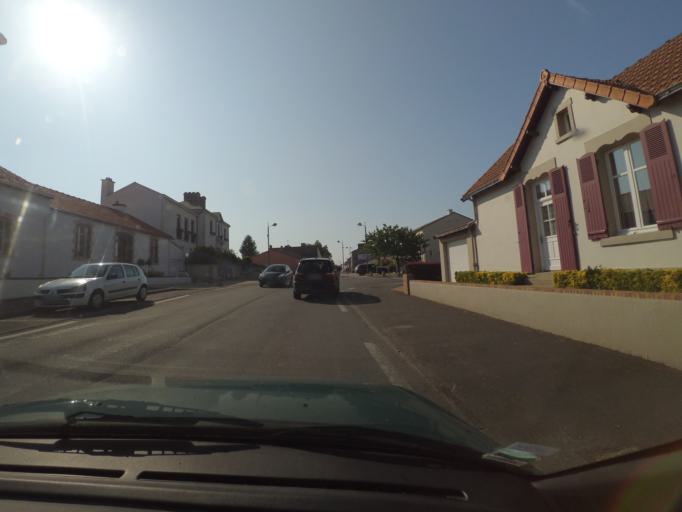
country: FR
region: Pays de la Loire
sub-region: Departement de la Loire-Atlantique
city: Le Pallet
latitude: 47.1399
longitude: -1.3379
